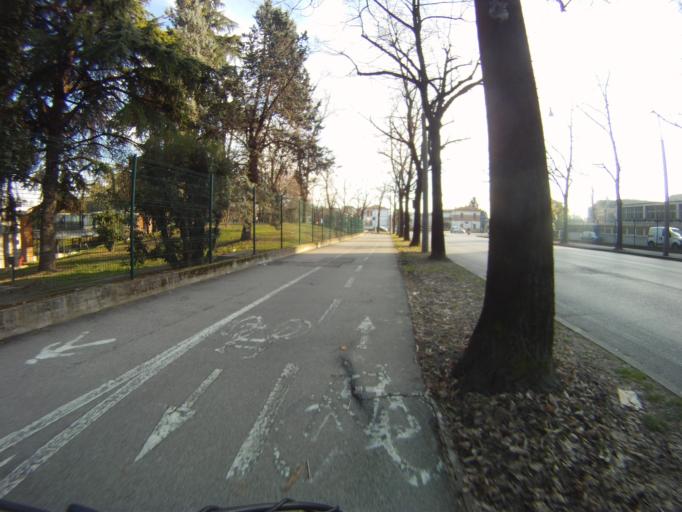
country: IT
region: Veneto
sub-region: Provincia di Padova
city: Padova
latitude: 45.4025
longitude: 11.8889
